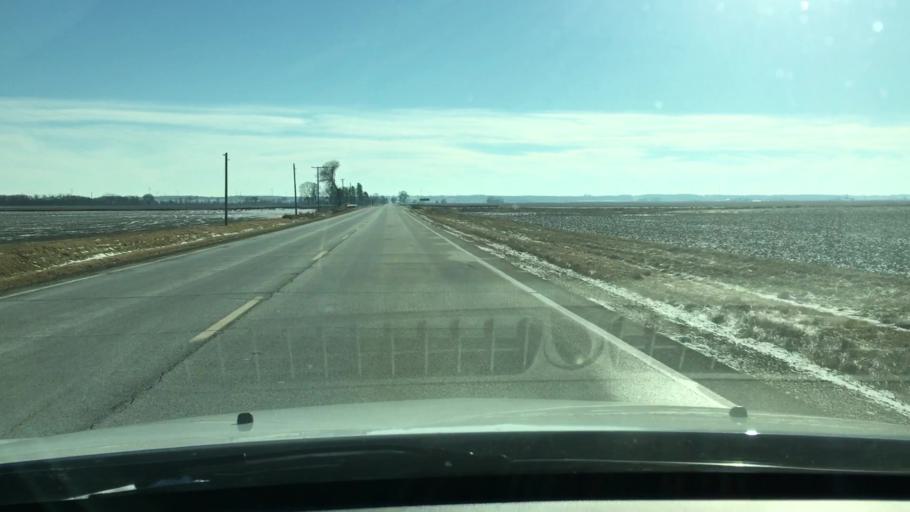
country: US
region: Illinois
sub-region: Ogle County
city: Rochelle
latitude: 41.7905
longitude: -89.0836
